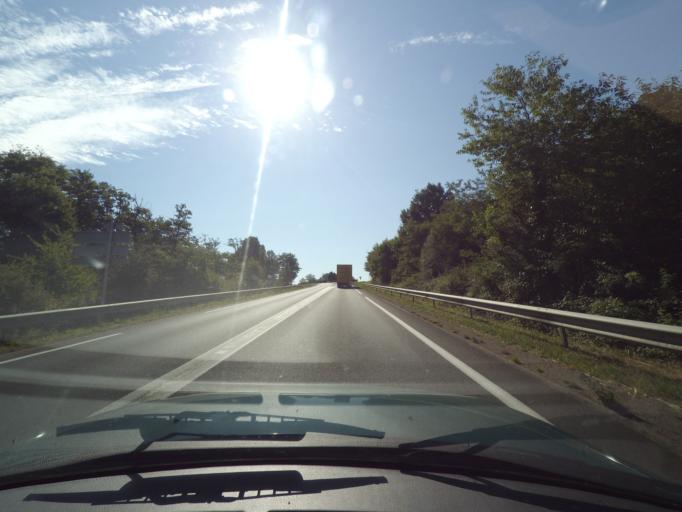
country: FR
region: Poitou-Charentes
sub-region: Departement de la Vienne
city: Lussac-les-Chateaux
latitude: 46.4234
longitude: 0.6310
